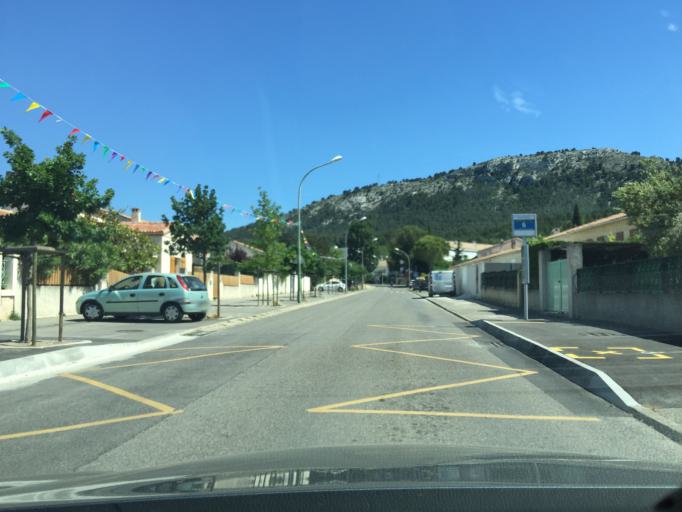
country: FR
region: Provence-Alpes-Cote d'Azur
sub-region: Departement des Bouches-du-Rhone
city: La Penne-sur-Huveaune
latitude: 43.2789
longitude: 5.5084
